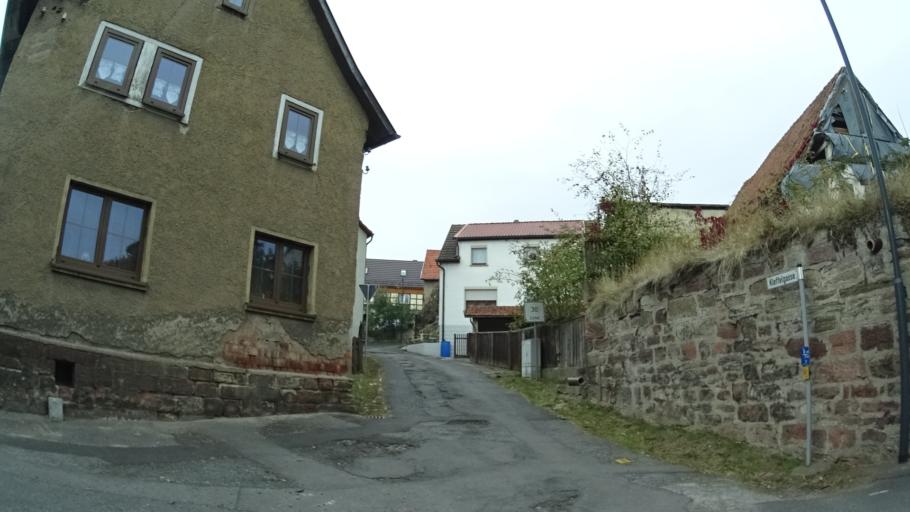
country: DE
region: Thuringia
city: Walldorf
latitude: 50.6114
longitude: 10.3883
